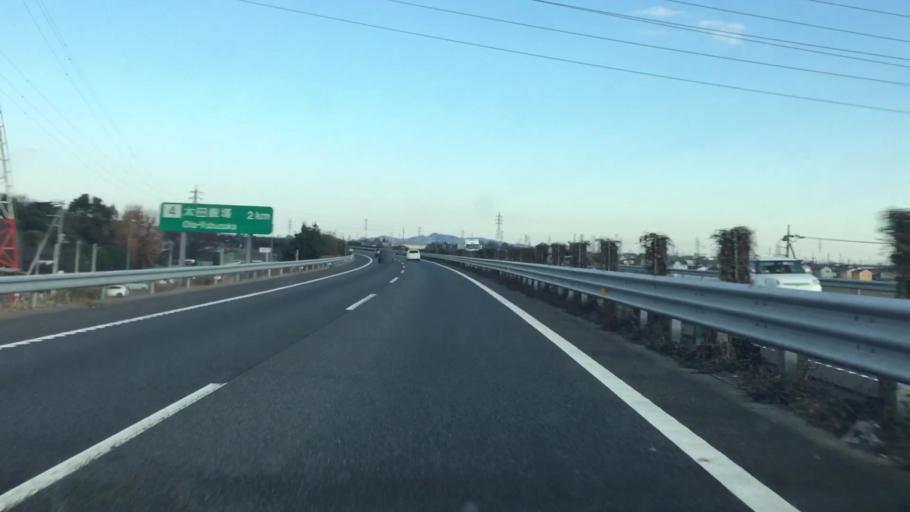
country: JP
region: Gunma
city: Isesaki
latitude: 36.3444
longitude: 139.2533
